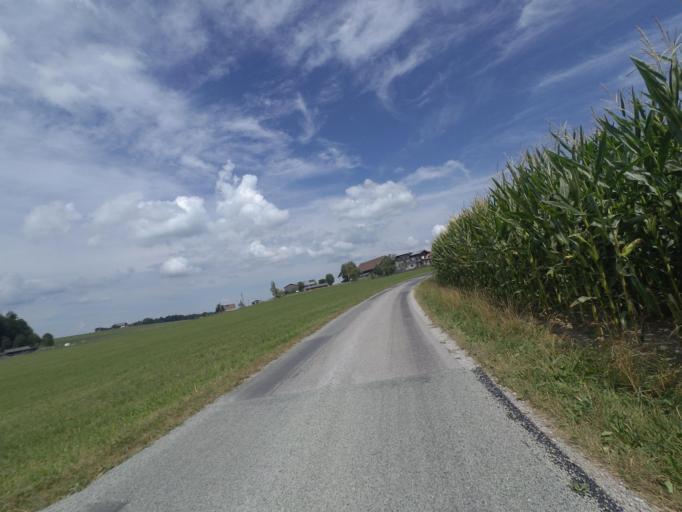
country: AT
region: Salzburg
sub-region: Politischer Bezirk Salzburg-Umgebung
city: Obertrum am See
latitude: 47.9026
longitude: 13.0920
